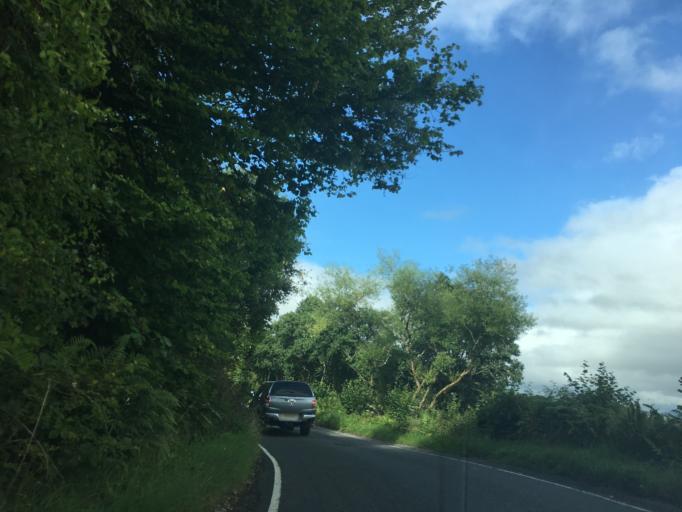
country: GB
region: Scotland
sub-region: Argyll and Bute
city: Ardrishaig
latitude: 56.0762
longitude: -5.5421
